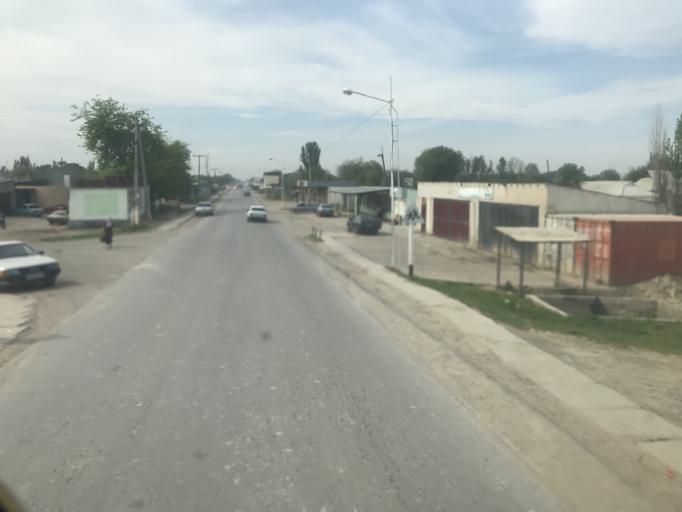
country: KZ
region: Ongtustik Qazaqstan
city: Asykata
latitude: 41.0076
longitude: 68.2156
